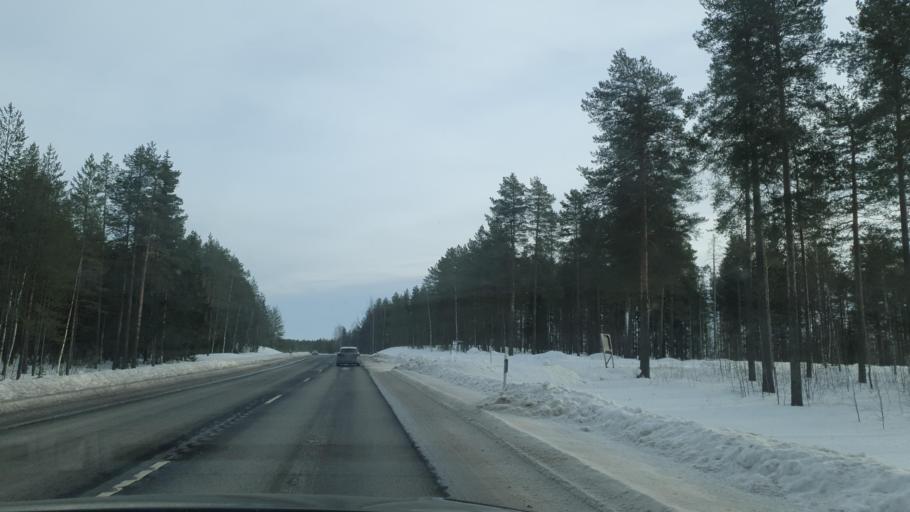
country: FI
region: Kainuu
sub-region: Kajaani
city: Vaala
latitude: 64.5728
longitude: 26.8543
